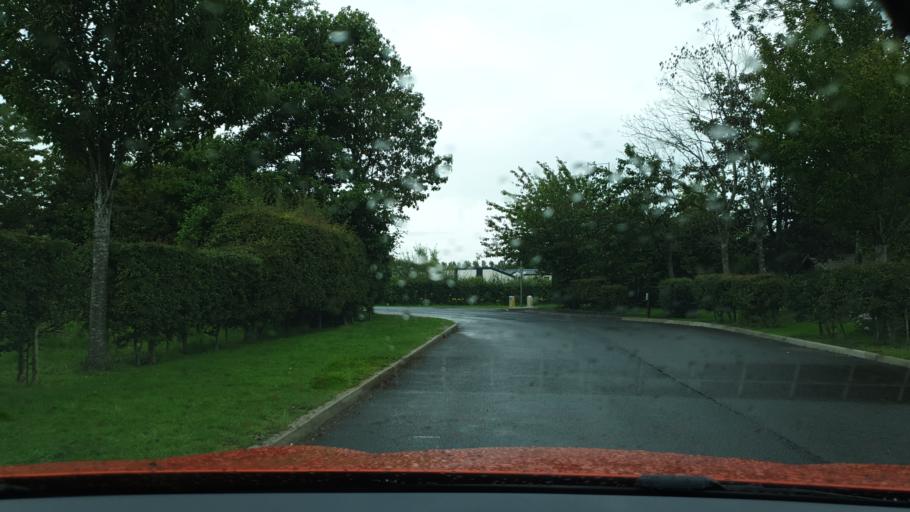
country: GB
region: England
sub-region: Lancashire
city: Carnforth
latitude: 54.1495
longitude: -2.7447
